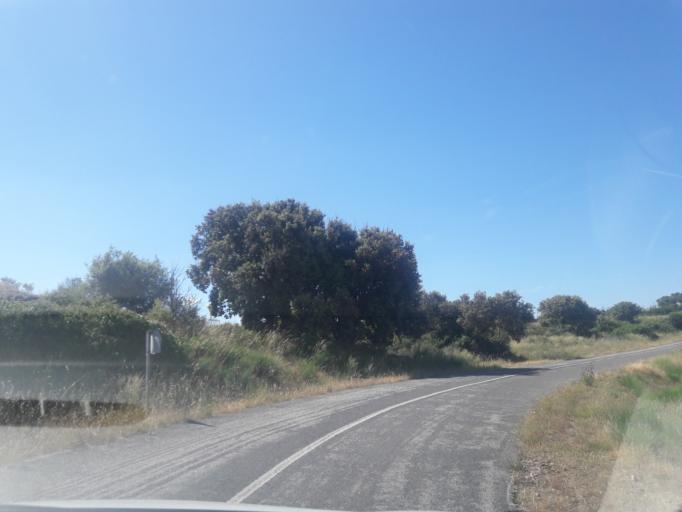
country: ES
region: Castille and Leon
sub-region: Provincia de Salamanca
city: Lumbrales
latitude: 40.9784
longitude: -6.7279
